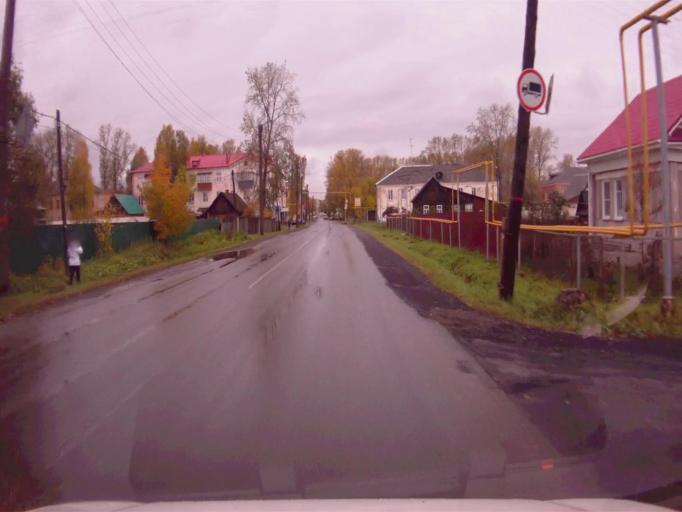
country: RU
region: Chelyabinsk
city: Verkhniy Ufaley
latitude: 56.0341
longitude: 60.2665
